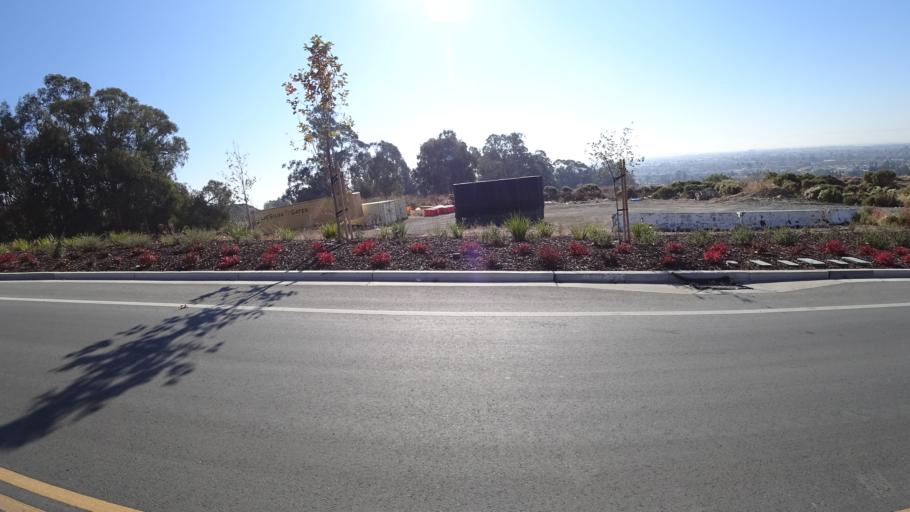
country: US
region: California
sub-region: Alameda County
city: Fairview
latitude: 37.6376
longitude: -122.0480
